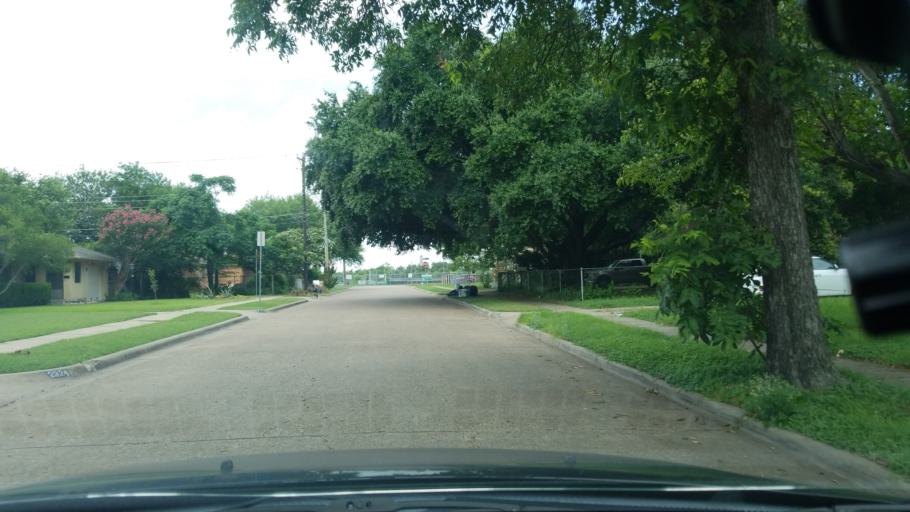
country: US
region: Texas
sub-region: Dallas County
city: Garland
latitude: 32.8282
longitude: -96.6778
